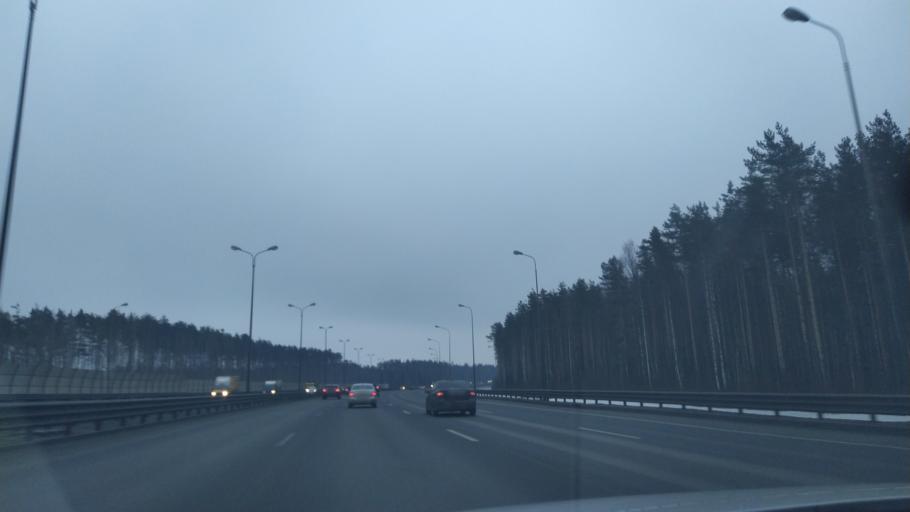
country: RU
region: St.-Petersburg
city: Krasnogvargeisky
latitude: 59.9721
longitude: 30.5465
